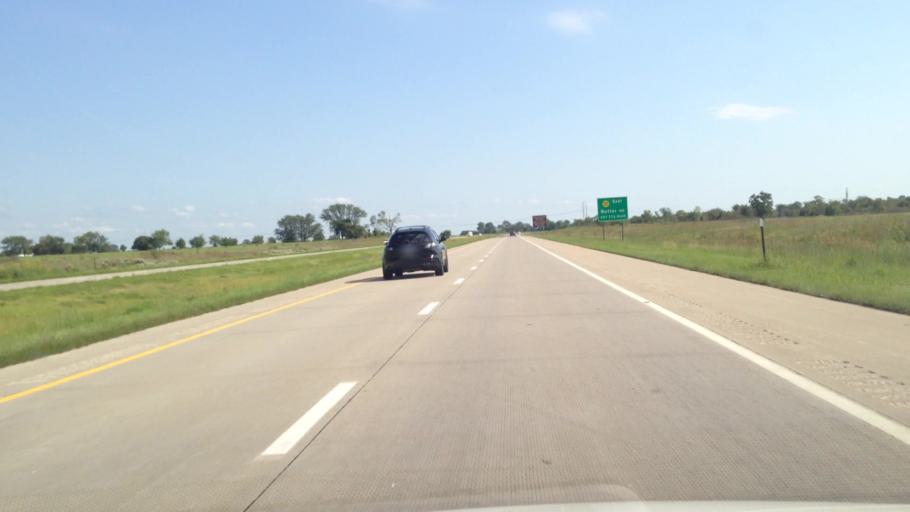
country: US
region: Kansas
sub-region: Linn County
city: La Cygne
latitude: 38.2831
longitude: -94.6720
